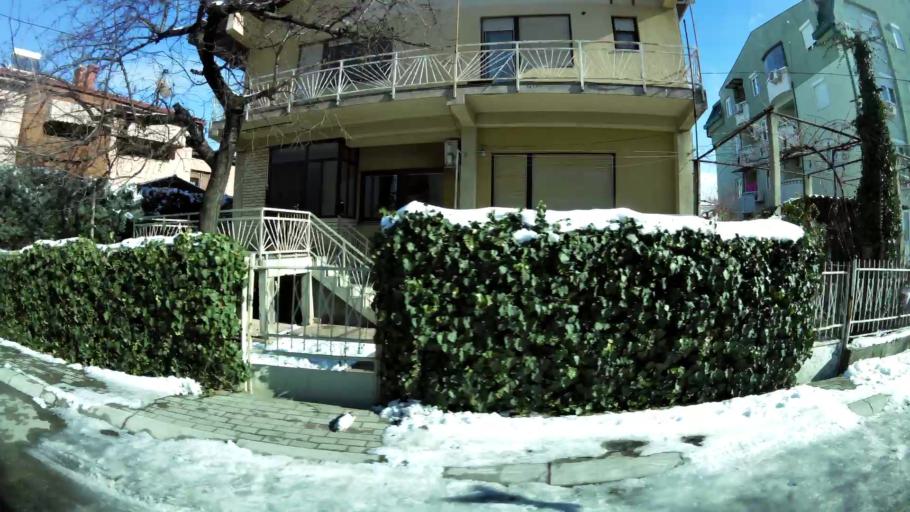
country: MK
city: Krushopek
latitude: 42.0043
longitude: 21.3604
